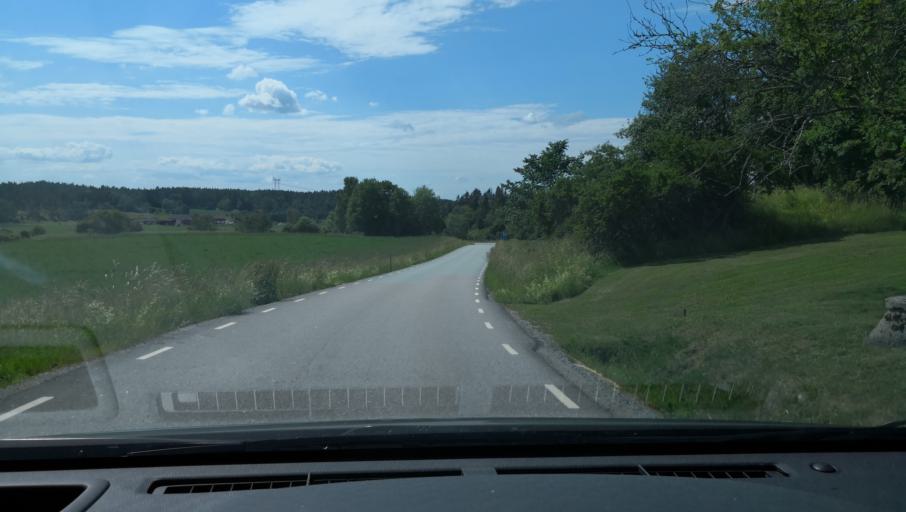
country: SE
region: Uppsala
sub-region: Habo Kommun
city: Balsta
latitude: 59.6665
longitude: 17.4507
